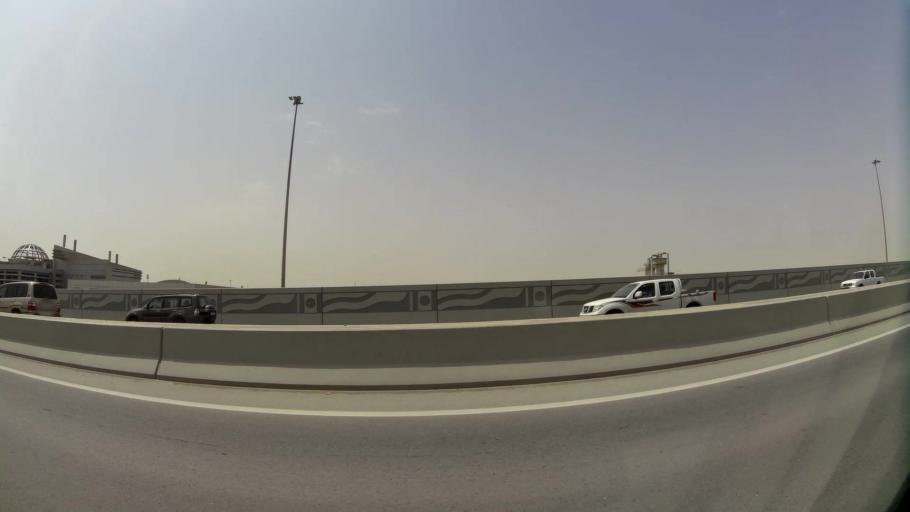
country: QA
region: Baladiyat ar Rayyan
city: Ar Rayyan
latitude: 25.2126
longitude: 51.4411
